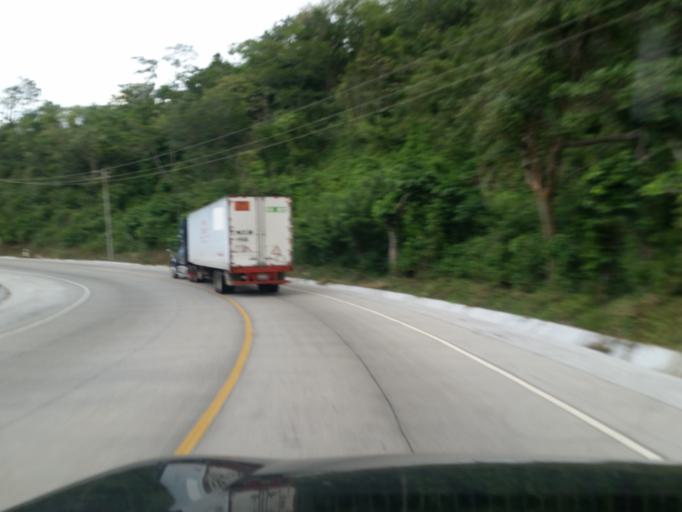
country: NI
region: Managua
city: Ciudad Sandino
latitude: 12.0800
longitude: -86.3779
